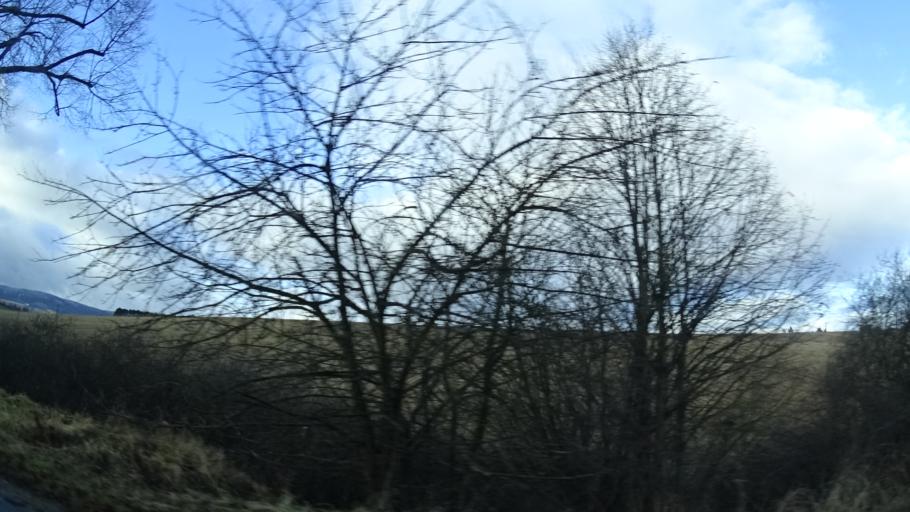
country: DE
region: Thuringia
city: Gossel
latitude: 50.7980
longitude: 10.8361
